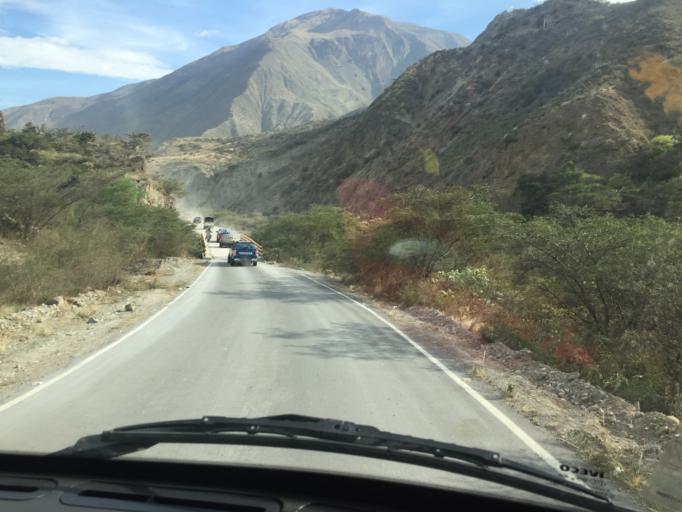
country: EC
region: Carchi
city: El Angel
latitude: 0.6041
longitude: -78.1379
